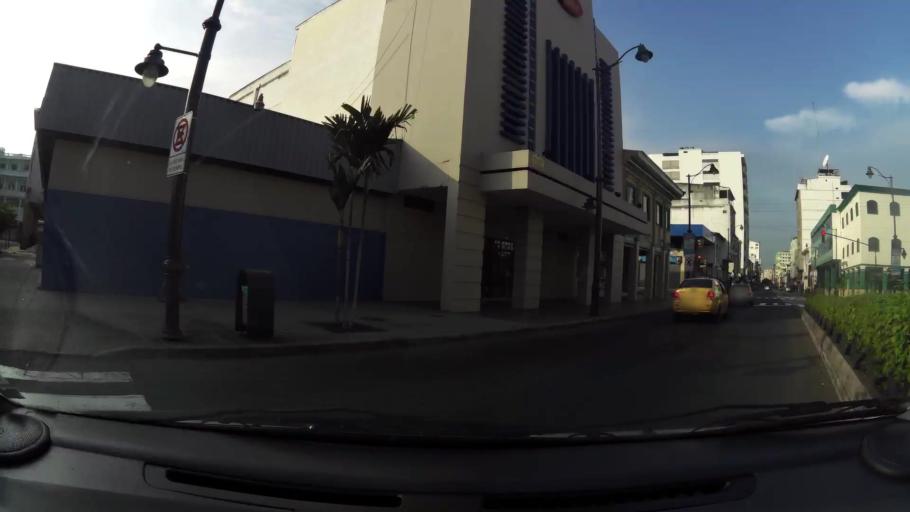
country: EC
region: Guayas
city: Eloy Alfaro
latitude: -2.1863
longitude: -79.8829
